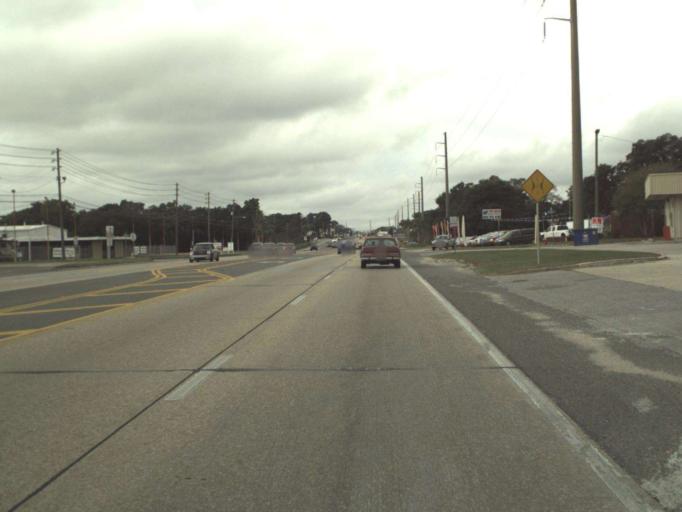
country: US
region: Florida
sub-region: Escambia County
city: West Pensacola
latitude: 30.4119
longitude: -87.2545
